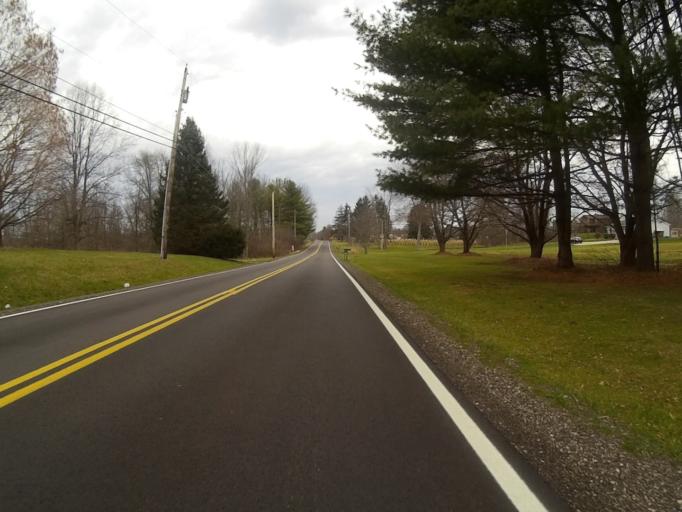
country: US
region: Ohio
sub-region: Portage County
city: Brimfield
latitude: 41.0678
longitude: -81.3287
